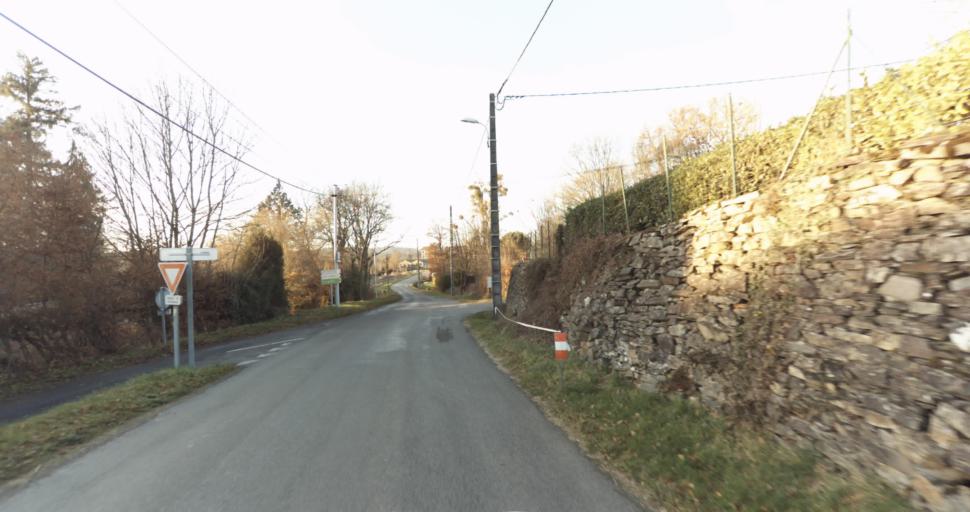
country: FR
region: Limousin
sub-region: Departement de la Haute-Vienne
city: Aixe-sur-Vienne
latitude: 45.8011
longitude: 1.1283
